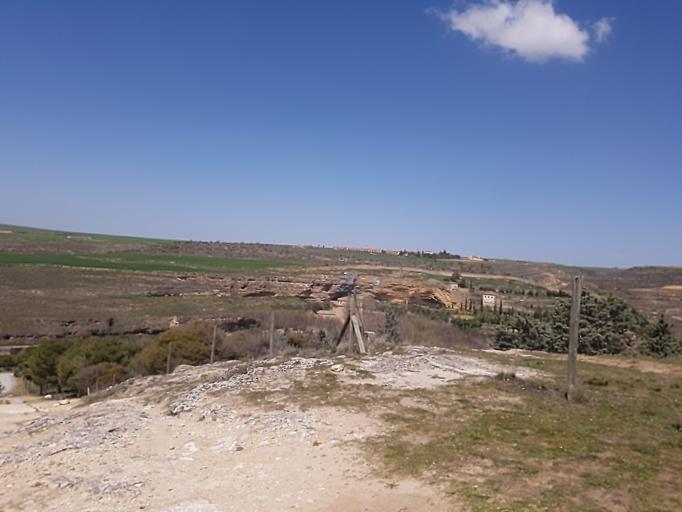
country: ES
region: Castille and Leon
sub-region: Provincia de Segovia
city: Segovia
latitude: 40.9526
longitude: -4.1350
